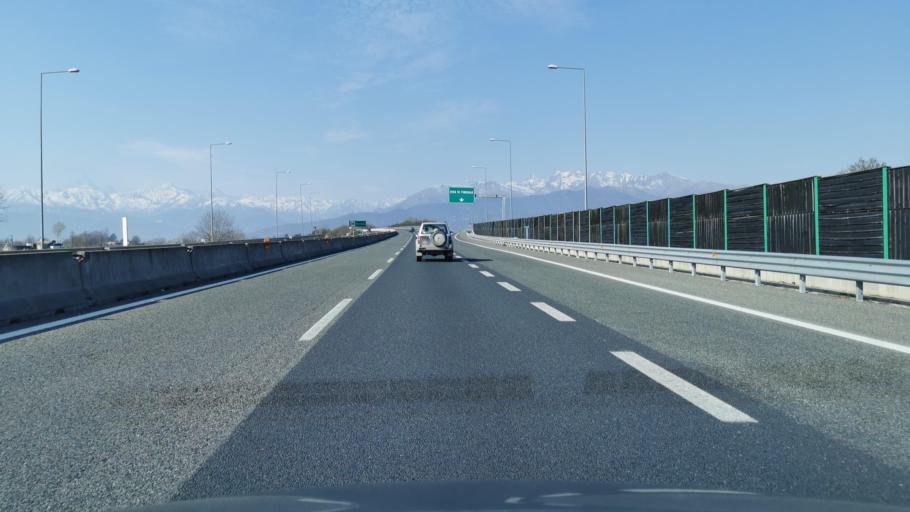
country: IT
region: Piedmont
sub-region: Provincia di Torino
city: Riva
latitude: 44.8975
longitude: 7.4057
